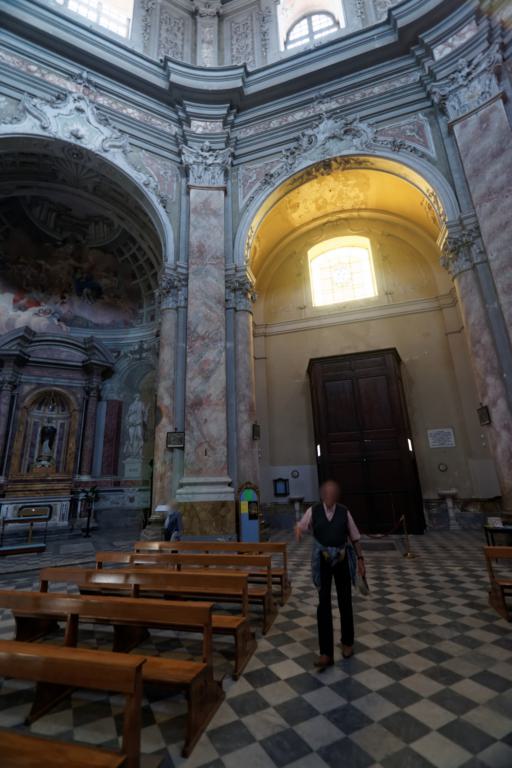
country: IT
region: Tuscany
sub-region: Provincia di Livorno
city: Livorno
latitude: 43.5548
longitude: 10.3083
